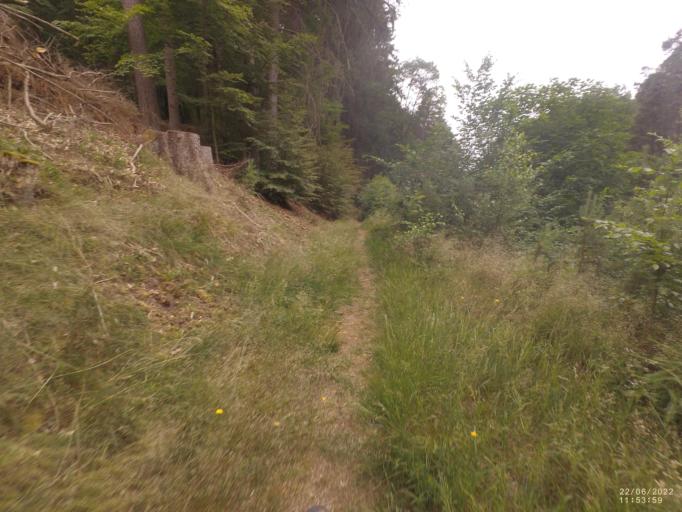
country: DE
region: Rheinland-Pfalz
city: Elmstein
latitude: 49.3339
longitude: 7.9304
